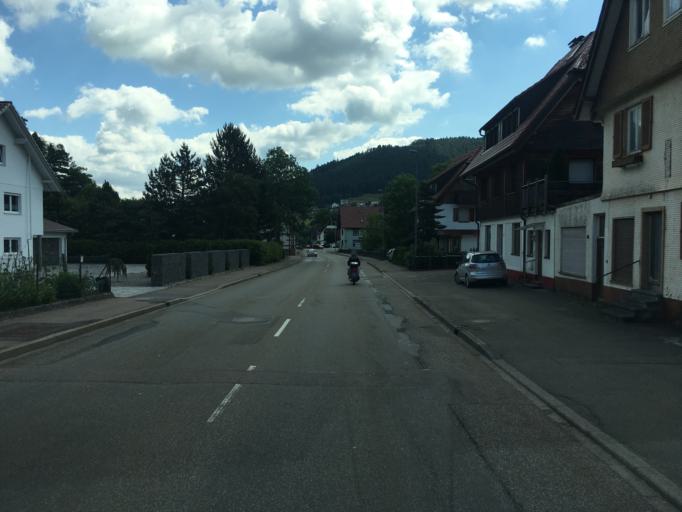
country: DE
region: Baden-Wuerttemberg
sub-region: Karlsruhe Region
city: Baiersbronn
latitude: 48.5100
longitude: 8.3673
